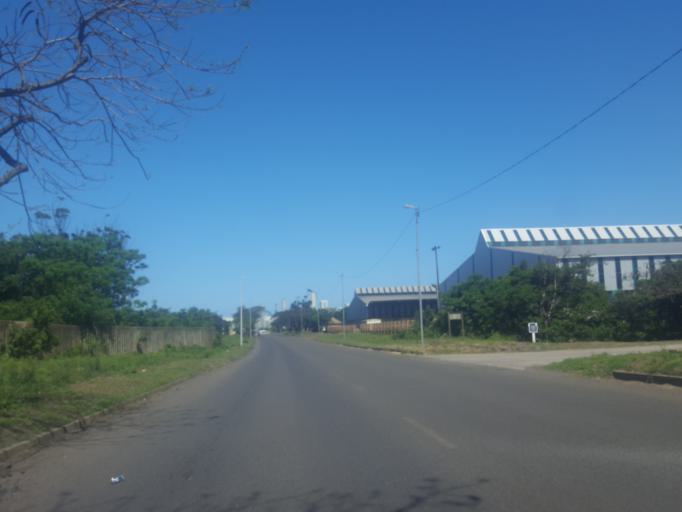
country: ZA
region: KwaZulu-Natal
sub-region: uThungulu District Municipality
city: Richards Bay
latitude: -28.7600
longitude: 32.0185
